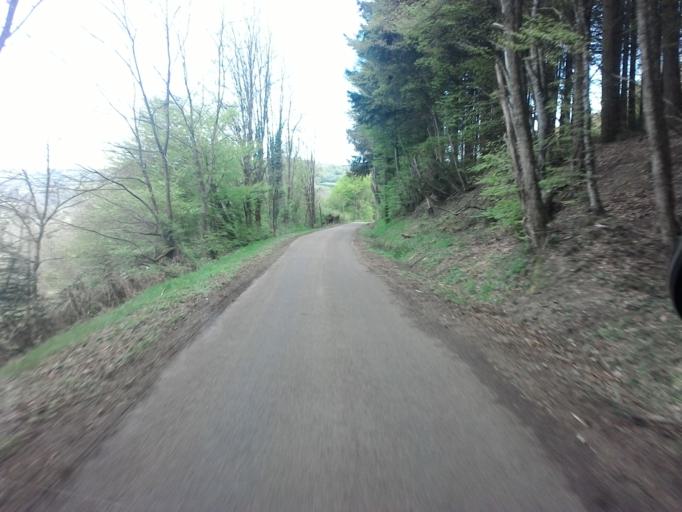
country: FR
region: Bourgogne
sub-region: Departement de la Nievre
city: Lormes
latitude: 47.3330
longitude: 3.9074
